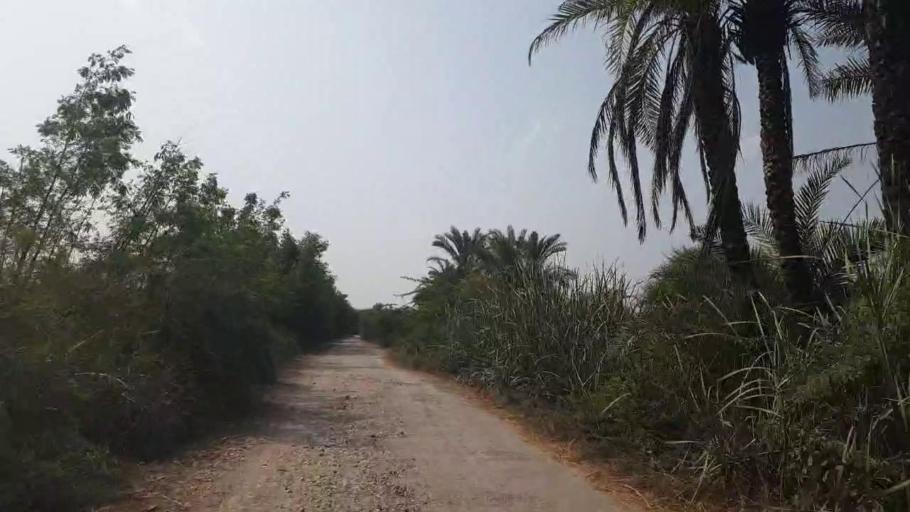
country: PK
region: Sindh
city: Badin
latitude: 24.7567
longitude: 68.7539
